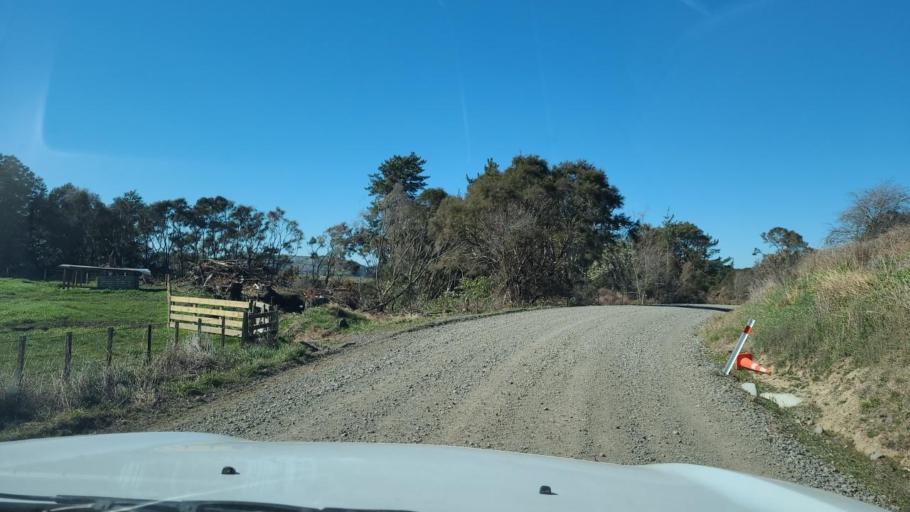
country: NZ
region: Hawke's Bay
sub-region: Napier City
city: Taradale
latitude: -39.4589
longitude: 176.5753
